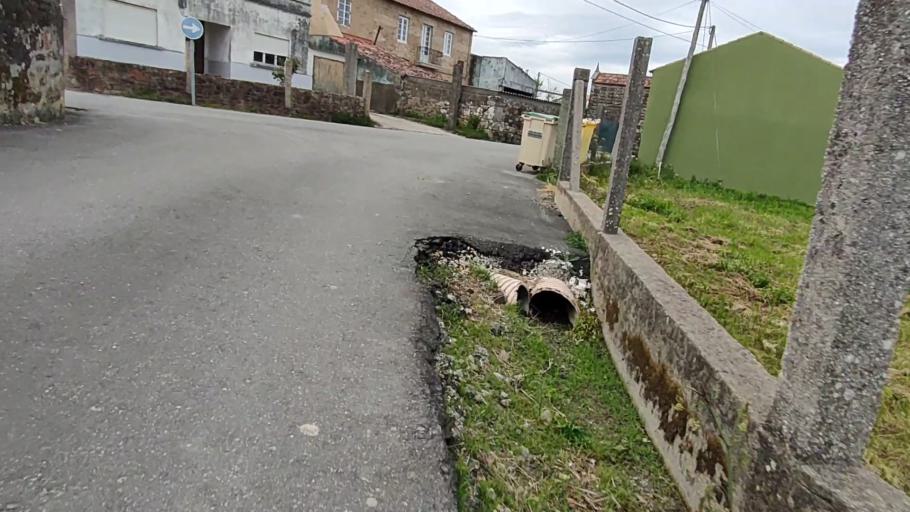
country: ES
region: Galicia
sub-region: Provincia da Coruna
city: Boiro
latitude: 42.6330
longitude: -8.8637
